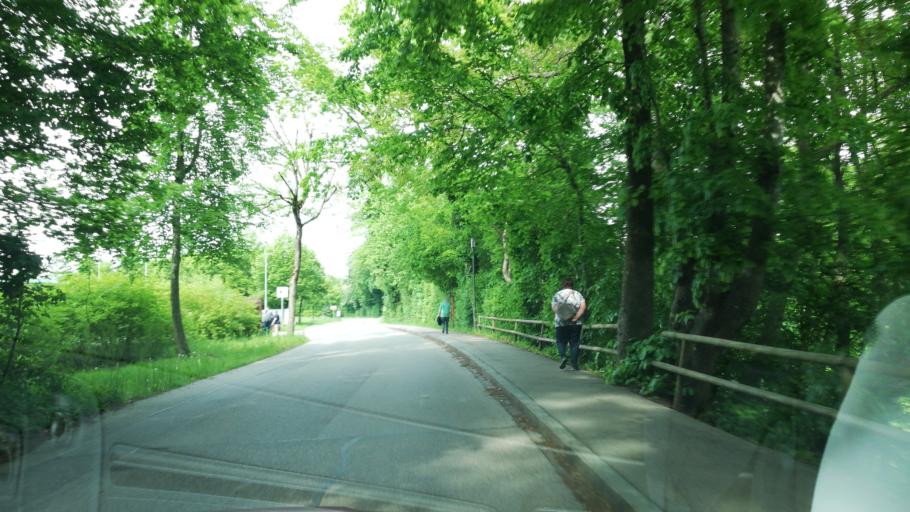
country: DE
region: Bavaria
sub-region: Upper Bavaria
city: Mehring
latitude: 48.1302
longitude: 12.7888
